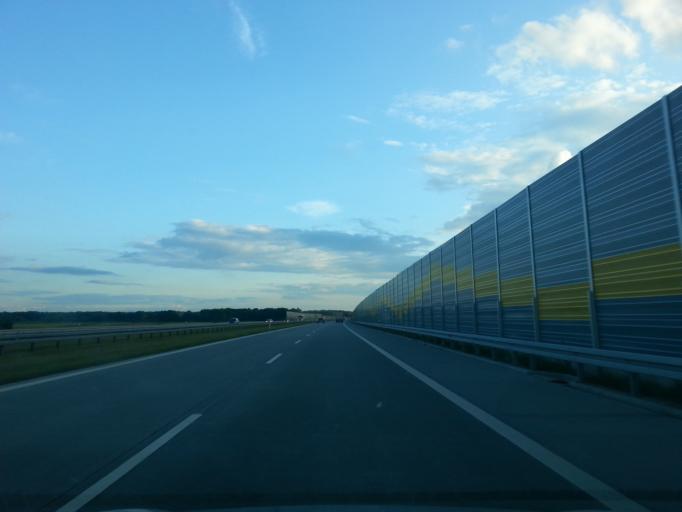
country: PL
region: Lodz Voivodeship
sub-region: Powiat sieradzki
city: Brzeznio
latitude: 51.4698
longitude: 18.6631
